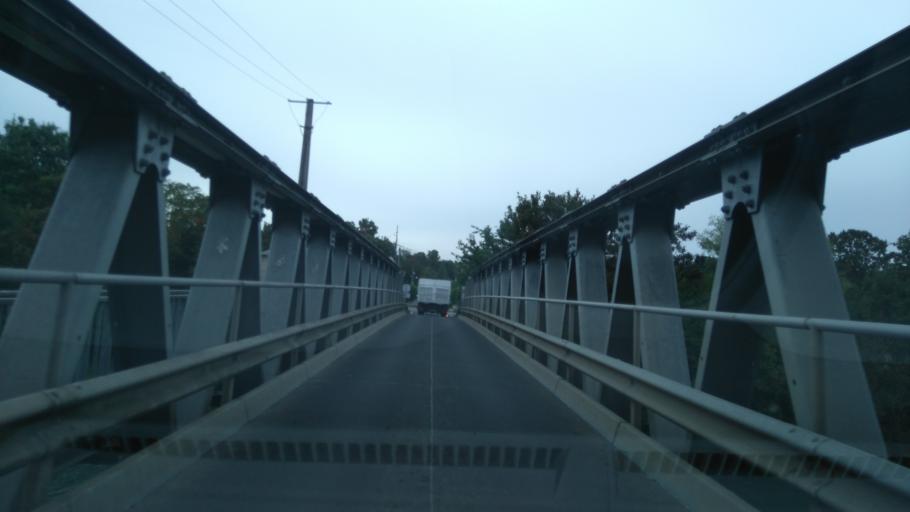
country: FR
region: Picardie
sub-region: Departement de l'Oise
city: Precy-sur-Oise
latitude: 49.2022
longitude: 2.3762
